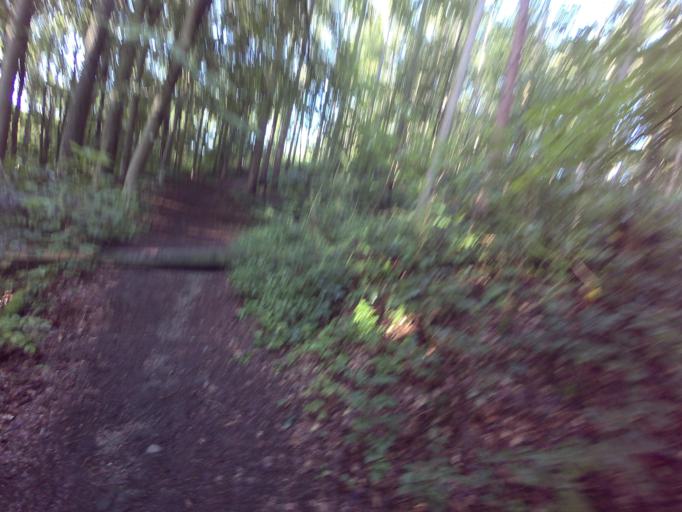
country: DE
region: North Rhine-Westphalia
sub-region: Regierungsbezirk Koln
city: Herzogenrath
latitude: 50.8421
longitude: 6.0951
